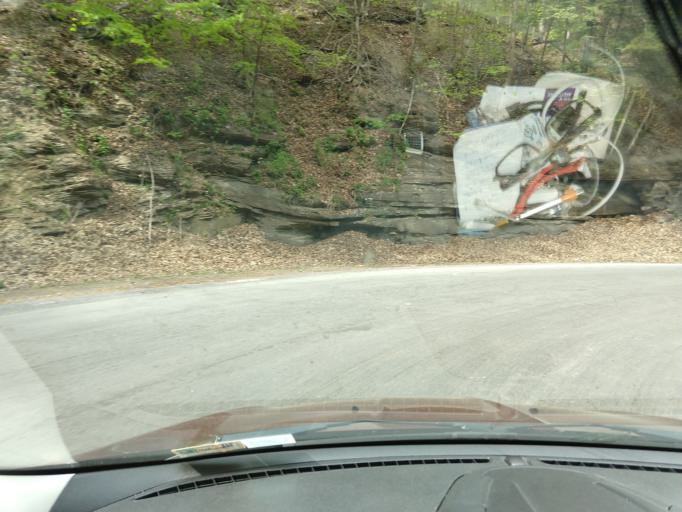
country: US
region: West Virginia
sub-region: McDowell County
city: Welch
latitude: 37.3660
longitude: -81.6429
